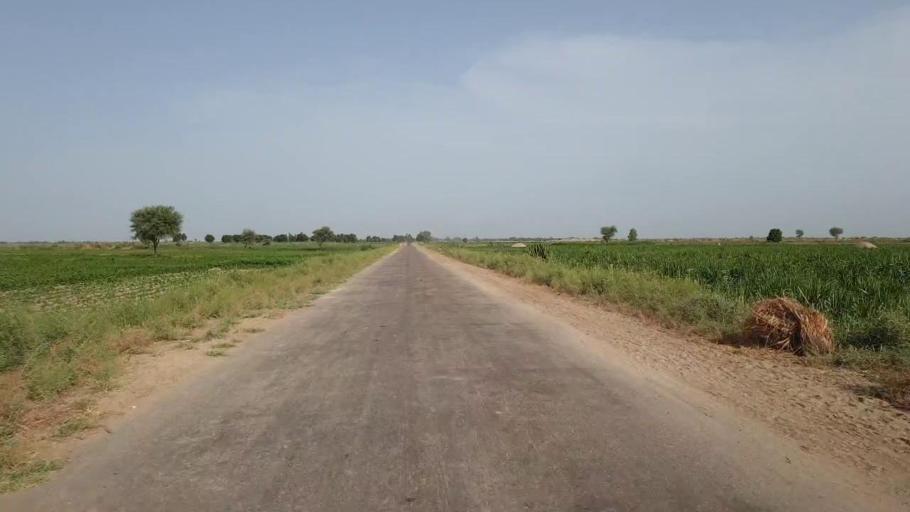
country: PK
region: Sindh
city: Sakrand
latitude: 26.2829
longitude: 68.2650
